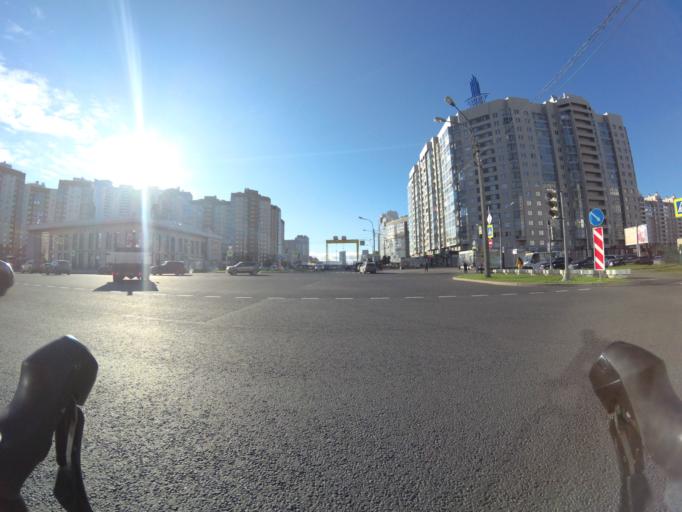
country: RU
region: Leningrad
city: Untolovo
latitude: 60.0017
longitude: 30.2094
